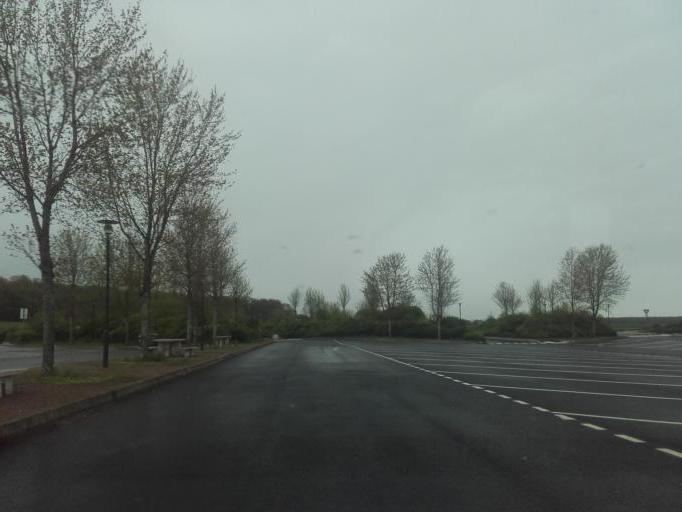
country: FR
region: Bourgogne
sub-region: Departement de l'Yonne
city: Avallon
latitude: 47.5024
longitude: 4.0382
